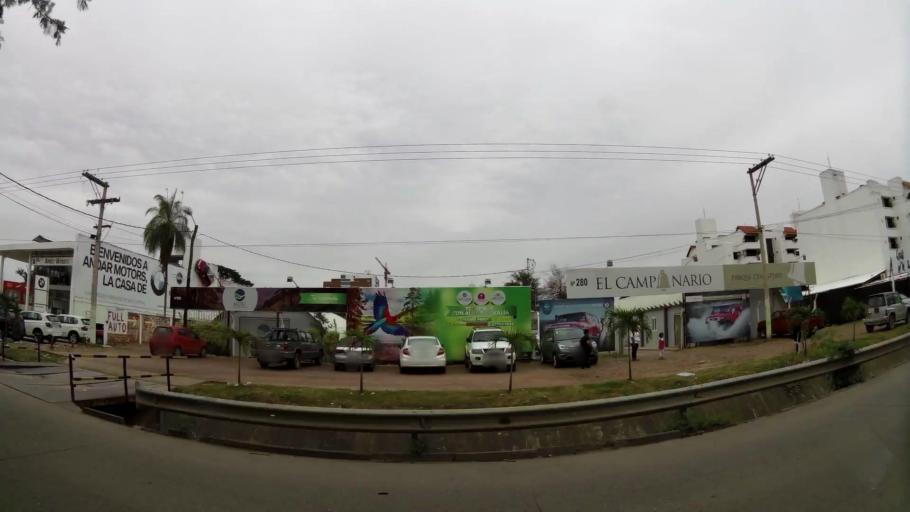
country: BO
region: Santa Cruz
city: Santa Cruz de la Sierra
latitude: -17.7615
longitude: -63.1938
